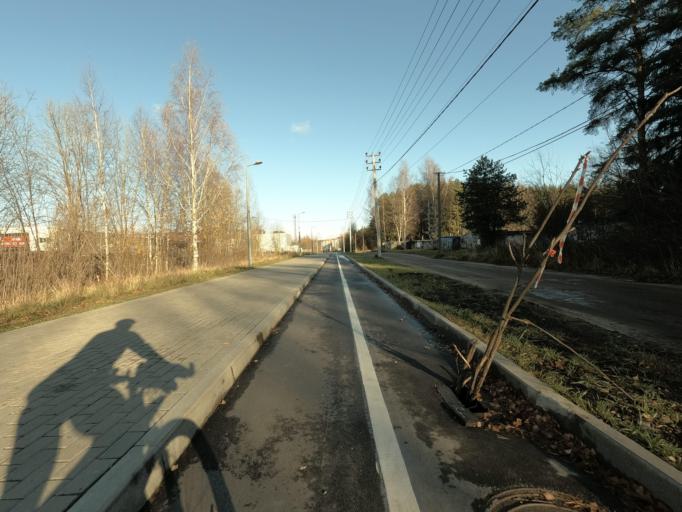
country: RU
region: Leningrad
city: Vsevolozhsk
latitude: 60.0239
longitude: 30.6122
